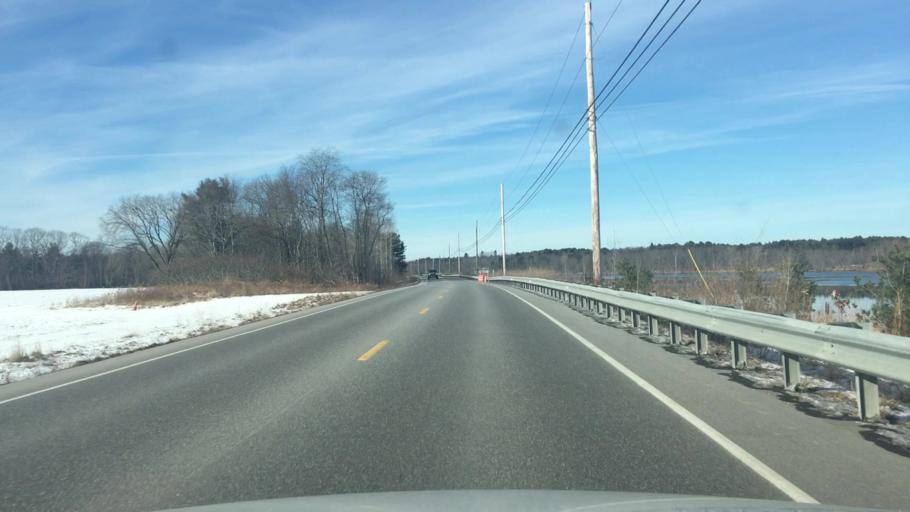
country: US
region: Maine
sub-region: Androscoggin County
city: Lisbon
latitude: 43.9920
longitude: -70.1403
